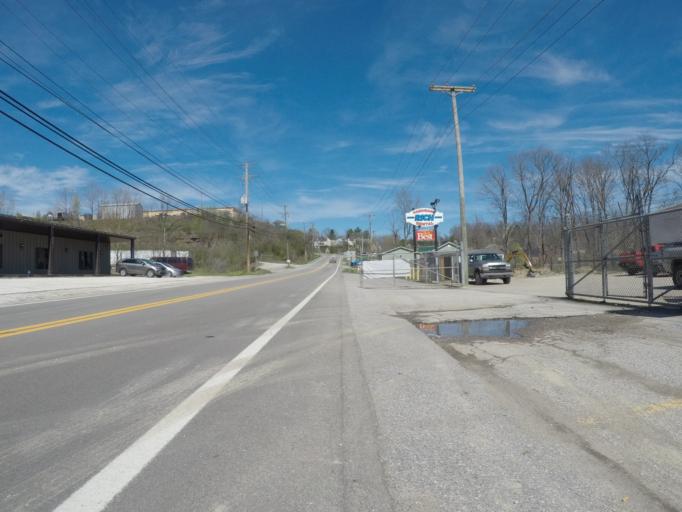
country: US
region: West Virginia
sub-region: Cabell County
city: Pea Ridge
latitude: 38.4092
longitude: -82.3202
